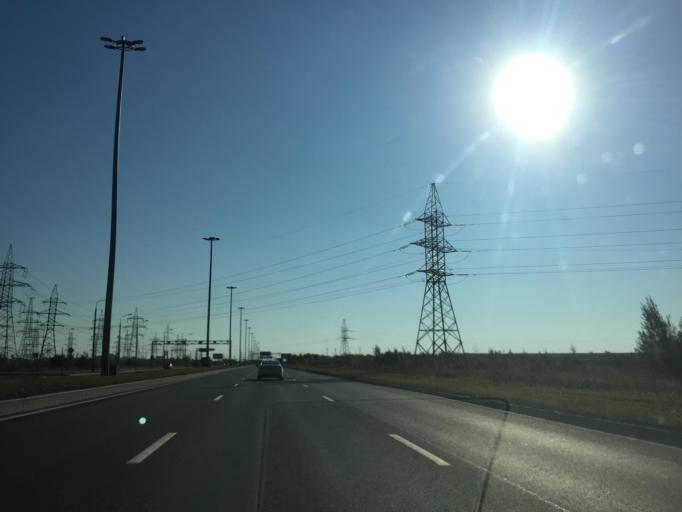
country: RU
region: St.-Petersburg
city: Petro-Slavyanka
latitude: 59.7546
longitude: 30.5211
